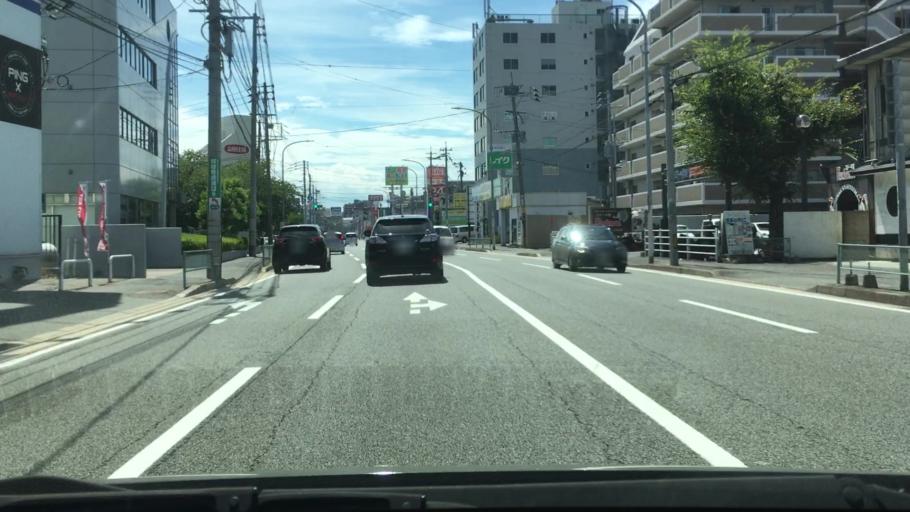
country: JP
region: Fukuoka
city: Onojo
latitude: 33.5536
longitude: 130.4553
